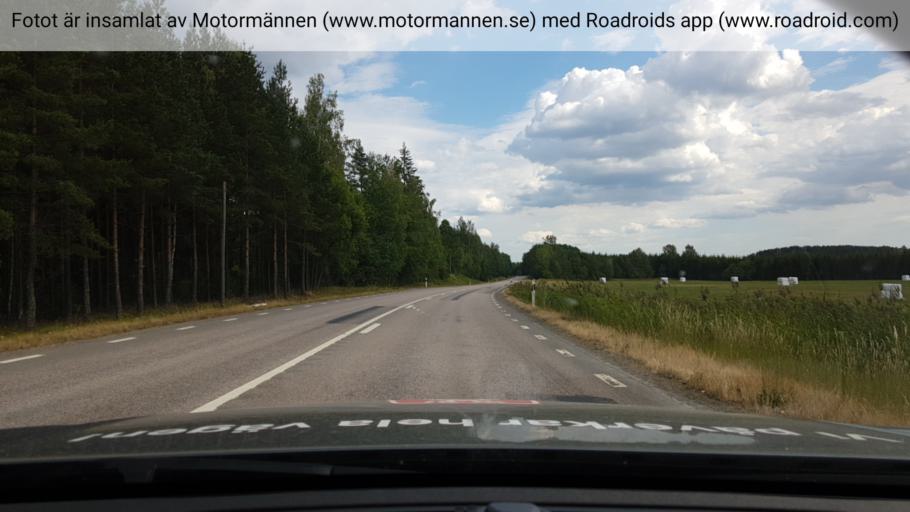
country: SE
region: Uppsala
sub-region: Heby Kommun
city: Morgongava
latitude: 59.9165
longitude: 17.0238
